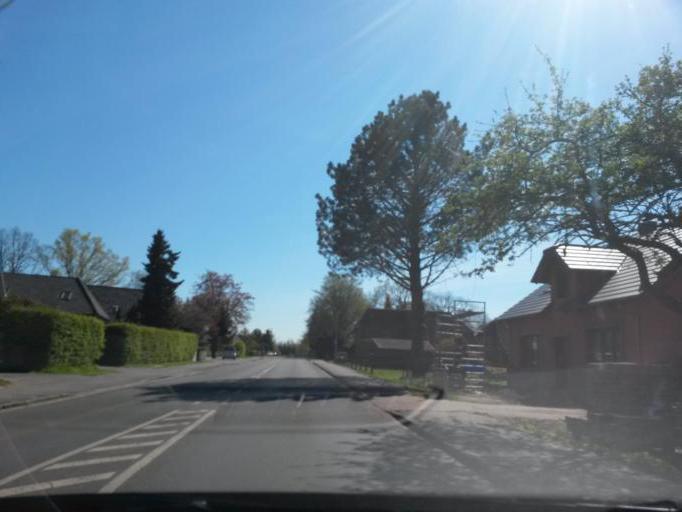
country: DE
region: Schleswig-Holstein
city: Rellingen
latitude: 53.6170
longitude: 9.8183
